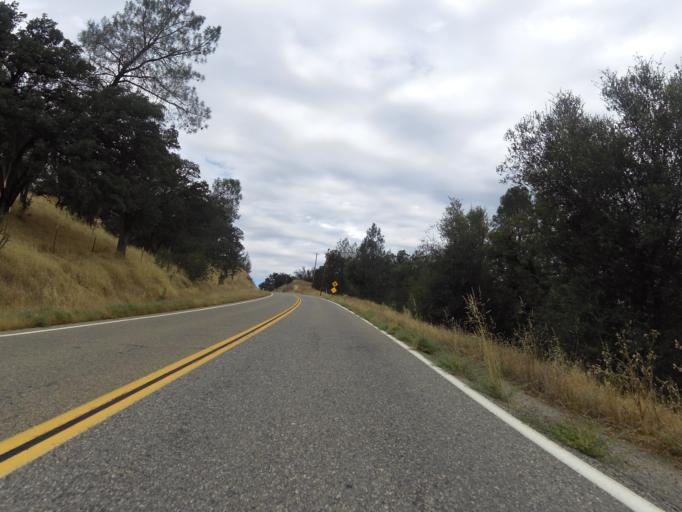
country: US
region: California
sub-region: Madera County
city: Yosemite Lakes
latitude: 37.2396
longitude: -119.7775
